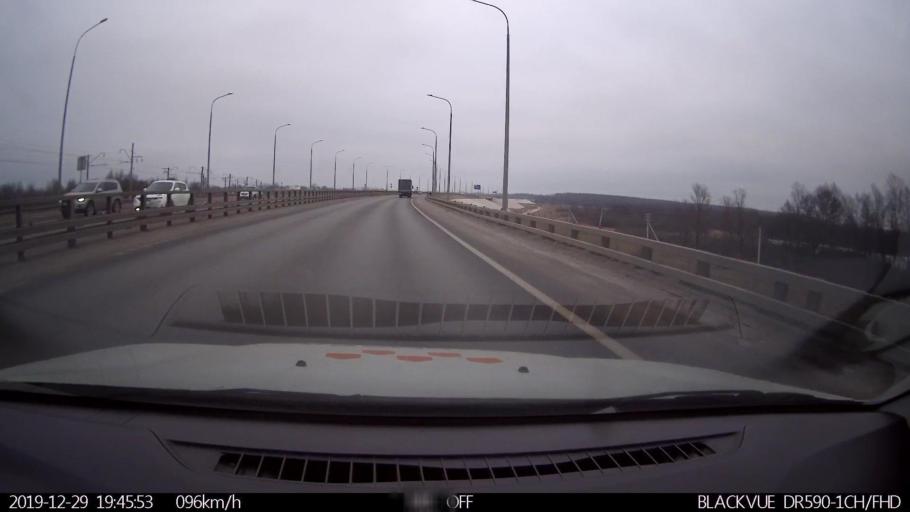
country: RU
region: Nizjnij Novgorod
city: Neklyudovo
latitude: 56.3894
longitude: 43.9727
